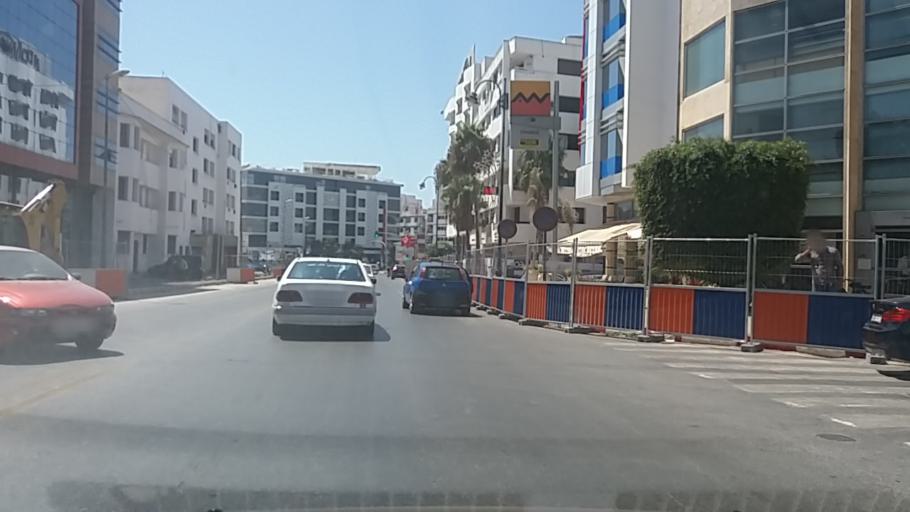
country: MA
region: Rabat-Sale-Zemmour-Zaer
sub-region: Rabat
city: Rabat
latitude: 34.0174
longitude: -6.8267
